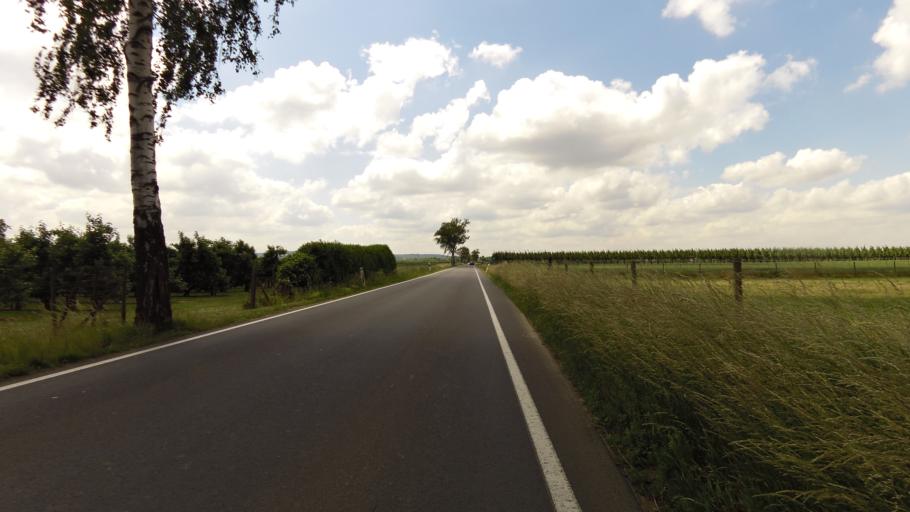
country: DE
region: North Rhine-Westphalia
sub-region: Regierungsbezirk Koln
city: Rheinbach
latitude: 50.6447
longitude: 6.9789
